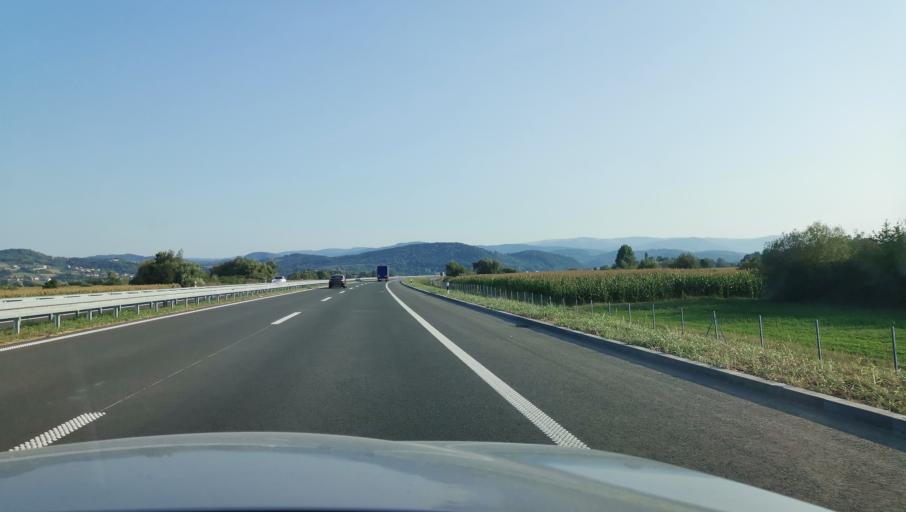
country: RS
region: Central Serbia
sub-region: Kolubarski Okrug
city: Ljig
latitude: 44.2602
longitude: 20.2709
